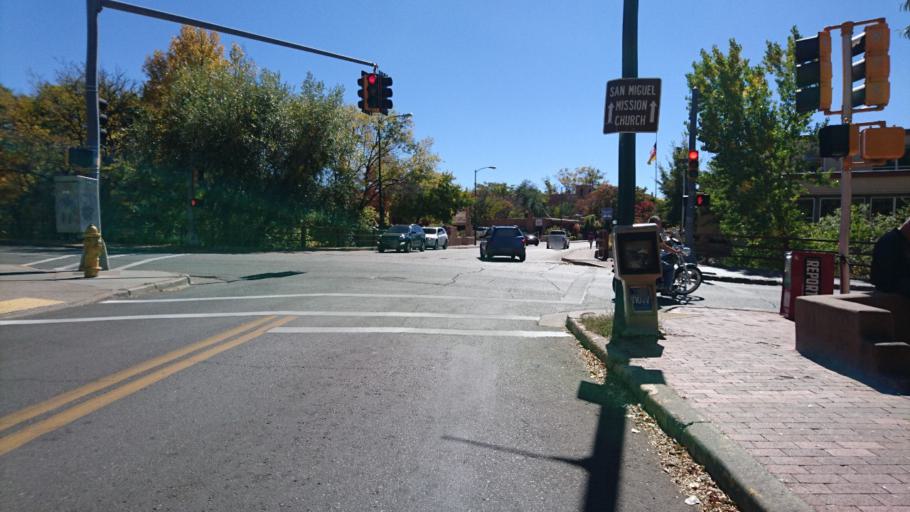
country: US
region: New Mexico
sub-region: Santa Fe County
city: Santa Fe
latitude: 35.6850
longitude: -105.9377
